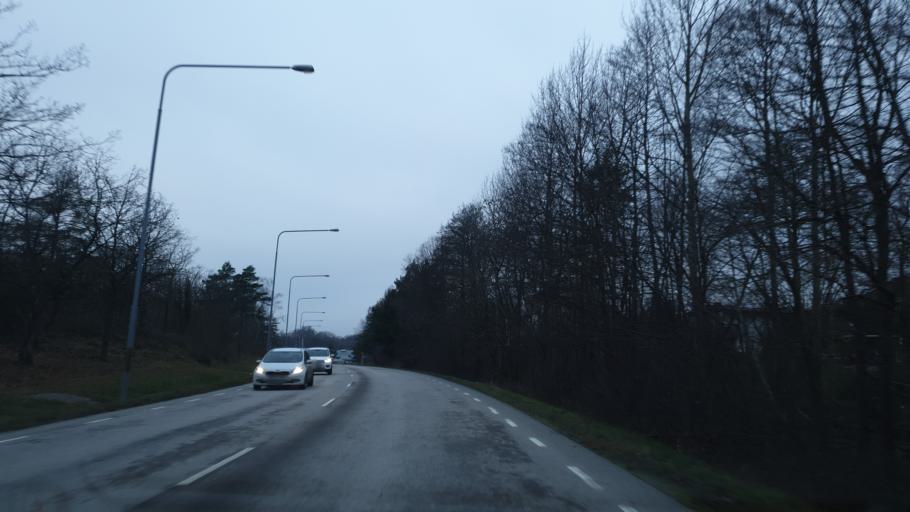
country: SE
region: Blekinge
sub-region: Karlskrona Kommun
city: Rodeby
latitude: 56.2089
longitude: 15.6486
